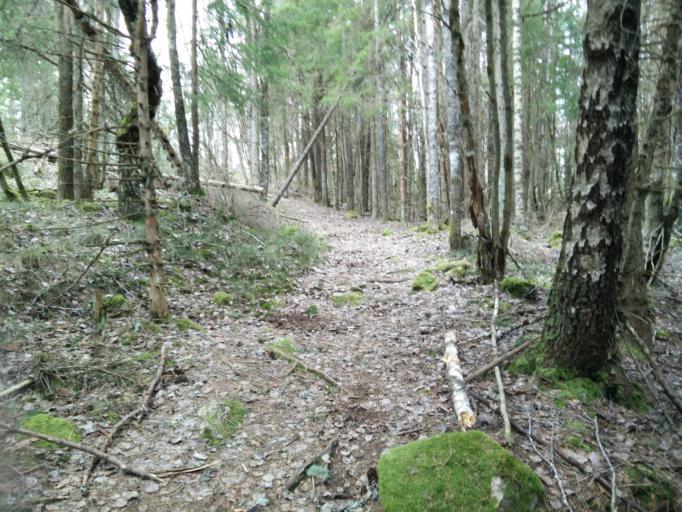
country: SE
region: OErebro
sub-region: Orebro Kommun
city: Garphyttan
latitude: 59.2864
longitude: 14.8927
